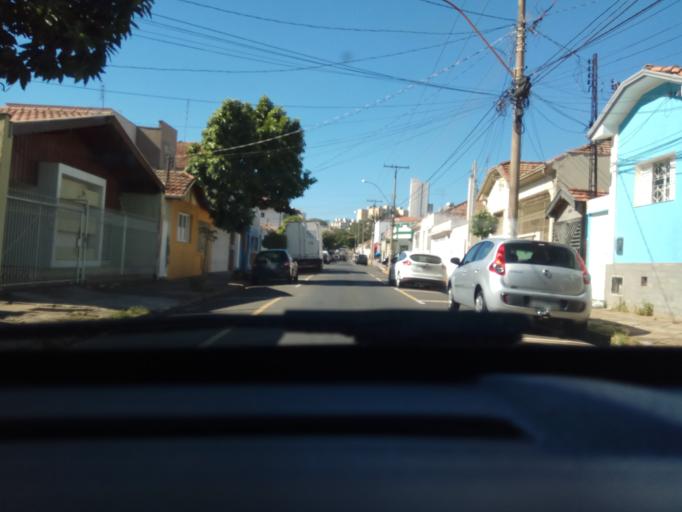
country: BR
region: Sao Paulo
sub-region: Piracicaba
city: Piracicaba
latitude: -22.7338
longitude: -47.6445
